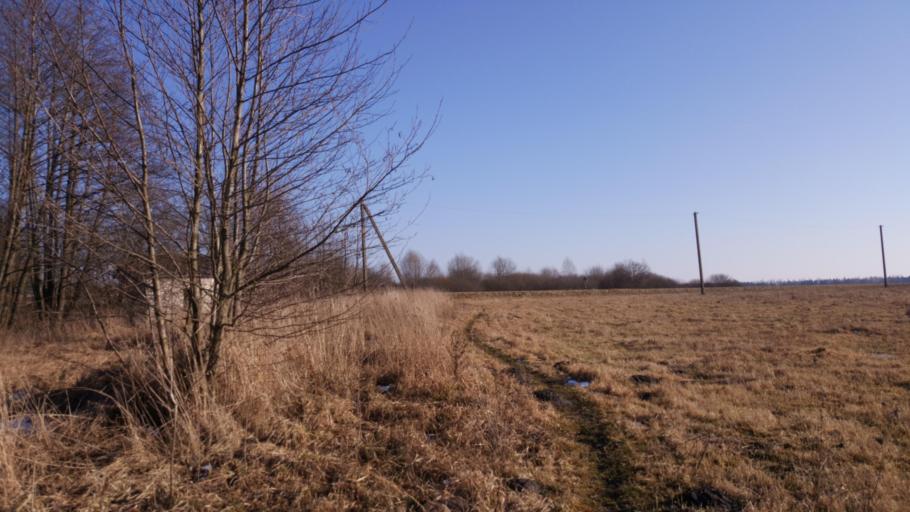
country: BY
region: Brest
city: Kamyanyets
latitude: 52.3864
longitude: 23.7863
